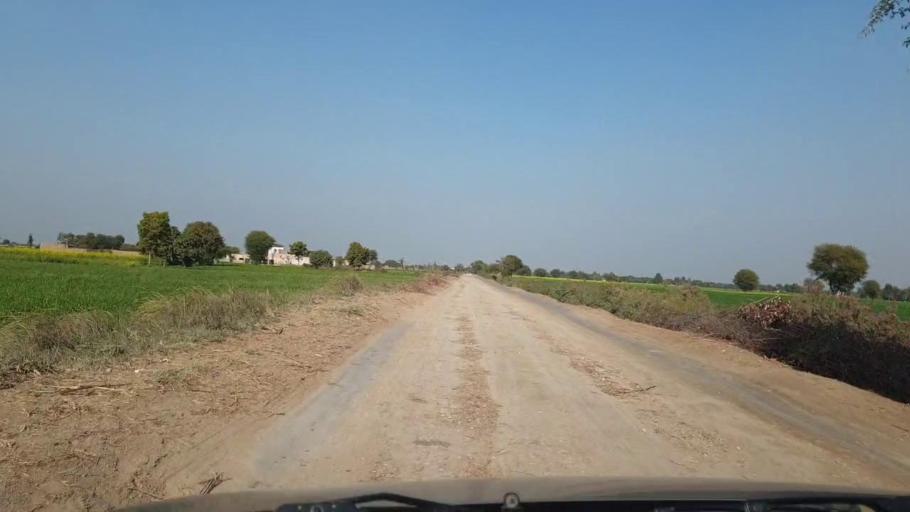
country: PK
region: Sindh
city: Jhol
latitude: 25.9330
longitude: 68.8777
